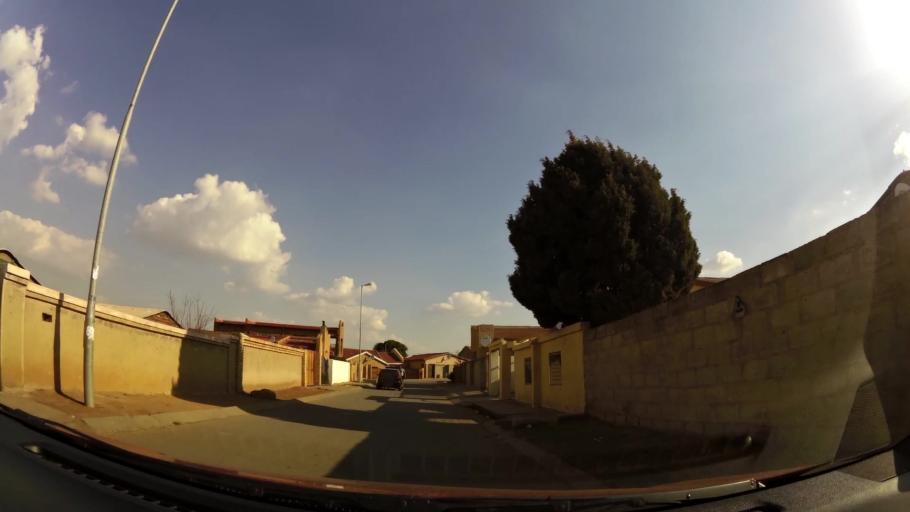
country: ZA
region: Gauteng
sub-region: City of Johannesburg Metropolitan Municipality
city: Soweto
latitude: -26.2328
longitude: 27.8651
